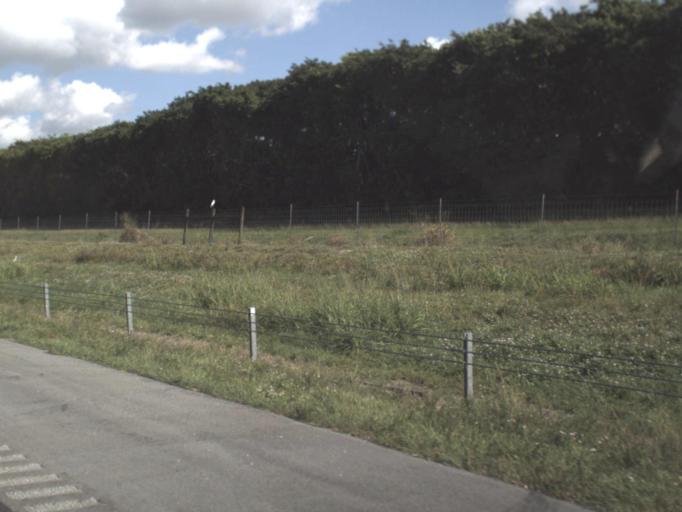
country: US
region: Florida
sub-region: Palm Beach County
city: Kings Point
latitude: 26.4178
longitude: -80.1714
